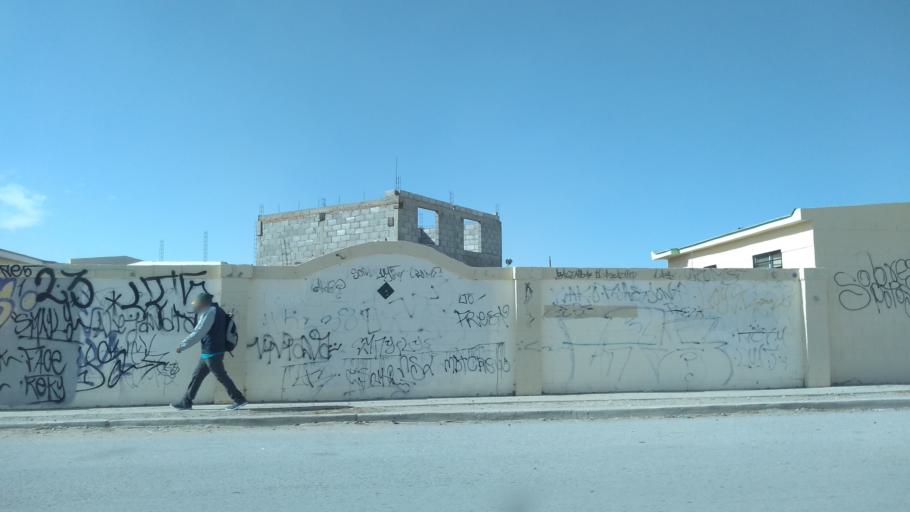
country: US
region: Texas
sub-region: El Paso County
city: San Elizario
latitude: 31.5681
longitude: -106.3319
